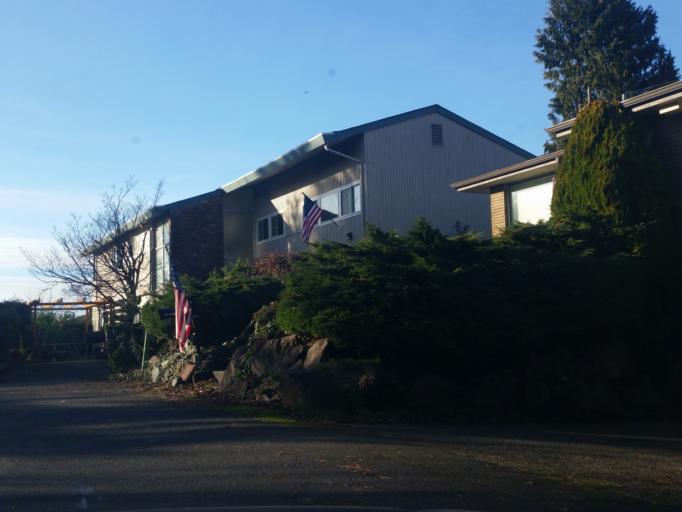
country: US
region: Washington
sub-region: King County
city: Shoreline
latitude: 47.6940
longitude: -122.3810
